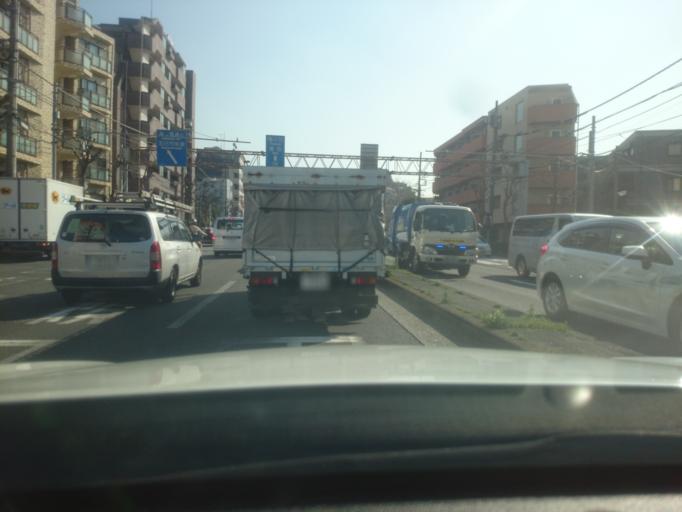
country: JP
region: Tokyo
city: Mitaka-shi
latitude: 35.6920
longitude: 139.6168
